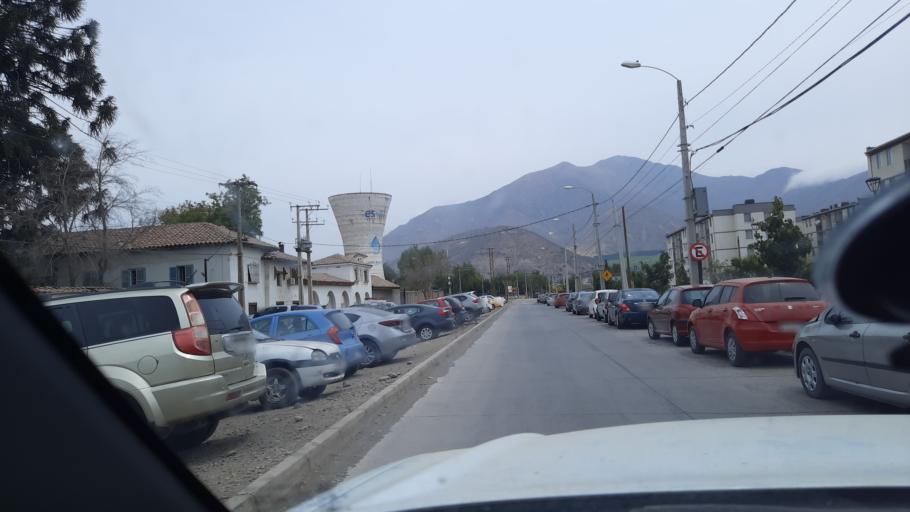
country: CL
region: Valparaiso
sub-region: Provincia de San Felipe
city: San Felipe
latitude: -32.7592
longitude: -70.7229
